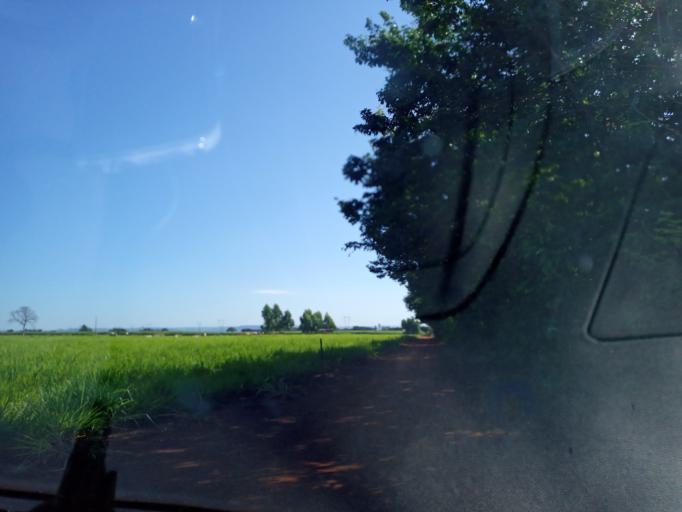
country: BR
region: Goias
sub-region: Itumbiara
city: Itumbiara
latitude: -18.4616
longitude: -49.1201
